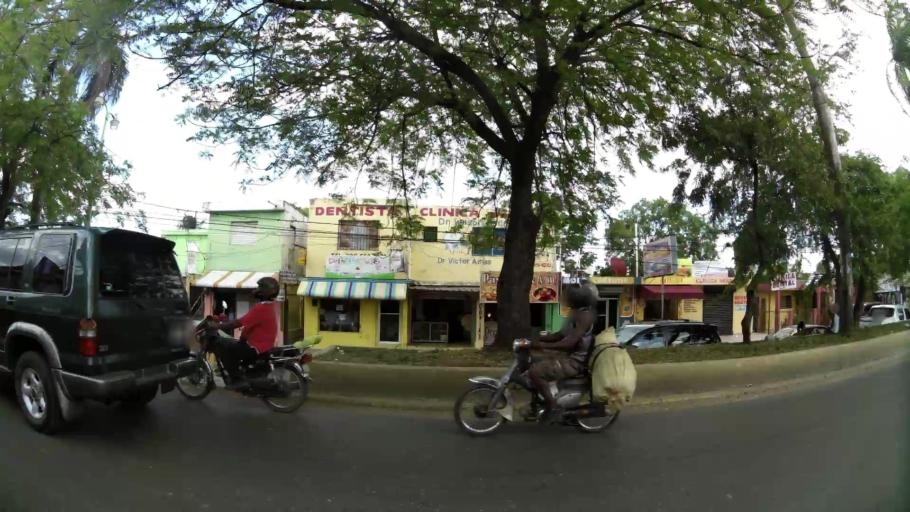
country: DO
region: Nacional
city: Ensanche Luperon
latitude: 18.5535
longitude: -69.9032
